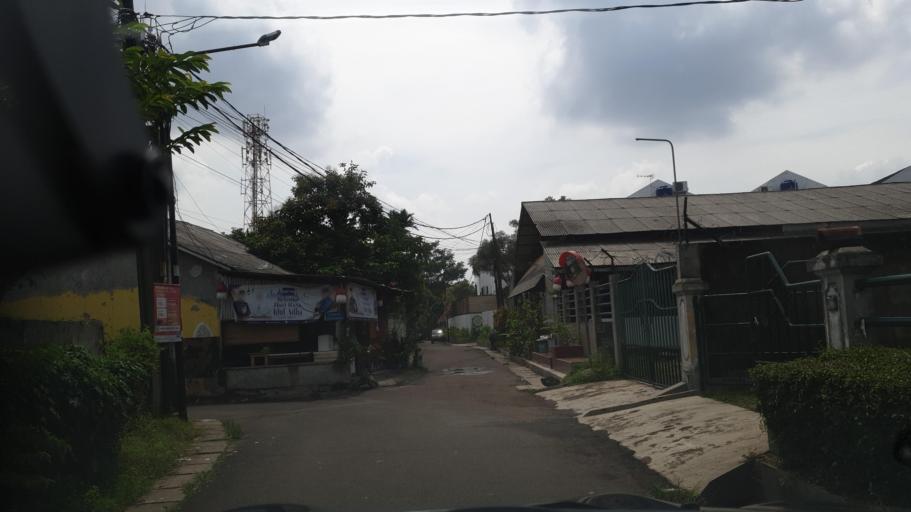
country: ID
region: West Java
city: Pamulang
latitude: -6.3407
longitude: 106.7675
